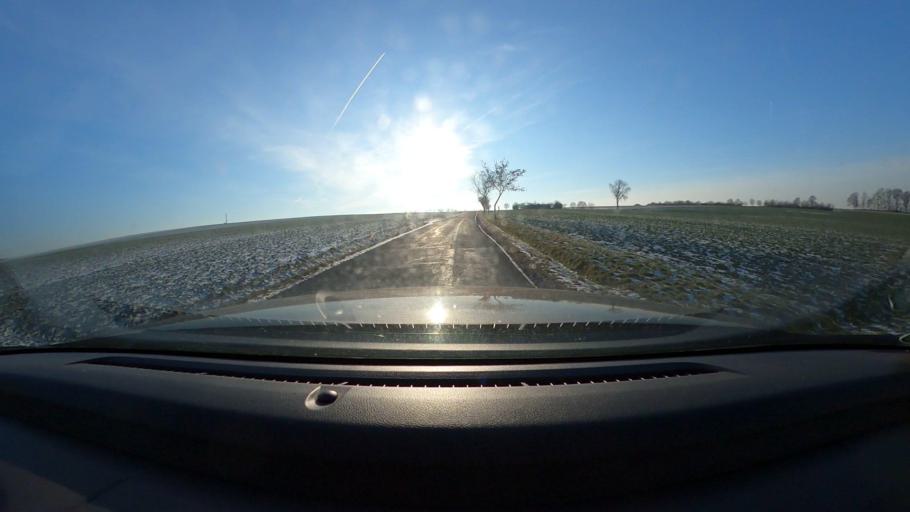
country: DE
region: Saxony
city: Grossschirma
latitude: 50.9526
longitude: 13.2329
